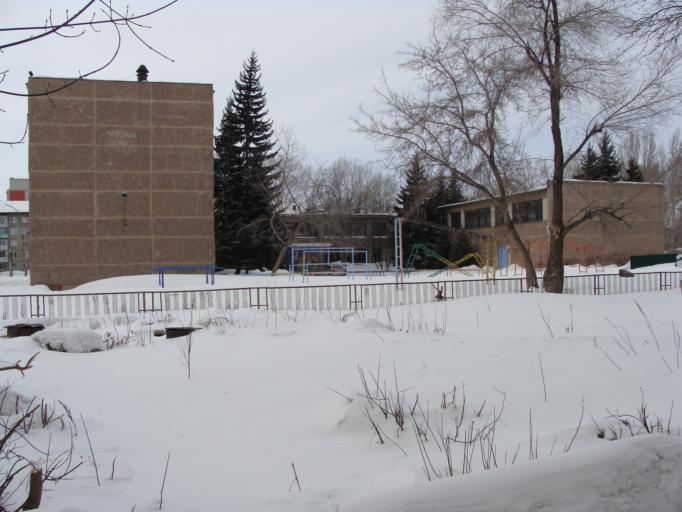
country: RU
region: Altai Krai
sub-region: Gorod Barnaulskiy
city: Barnaul
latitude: 53.3624
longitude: 83.6850
